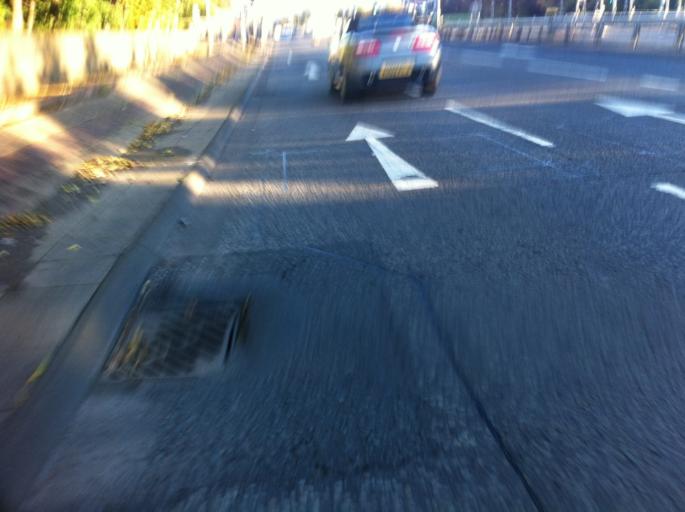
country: GB
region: Scotland
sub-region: Glasgow City
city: Glasgow
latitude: 55.8746
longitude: -4.2329
